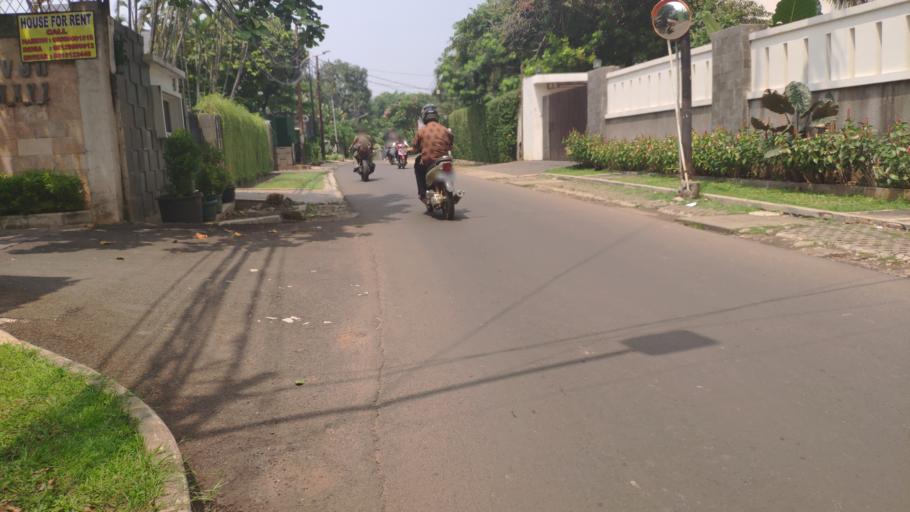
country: ID
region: Jakarta Raya
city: Jakarta
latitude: -6.2757
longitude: 106.8244
